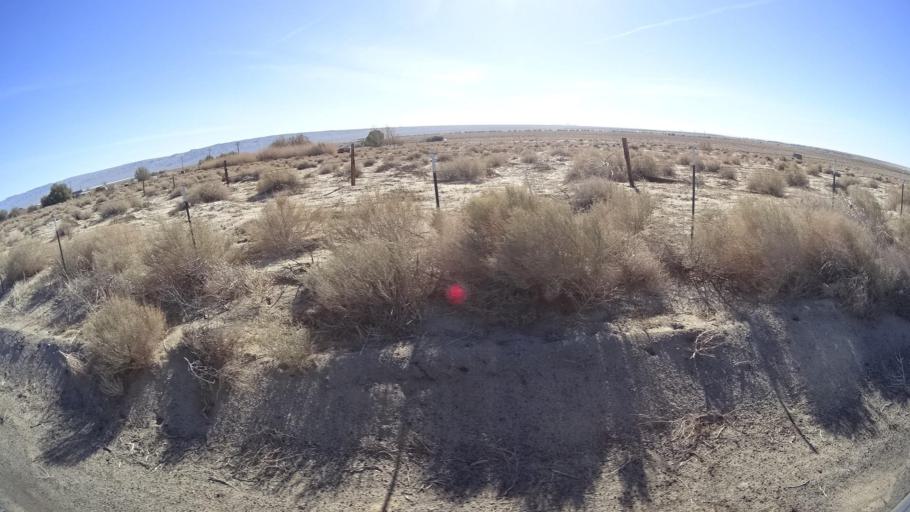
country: US
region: California
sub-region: Kern County
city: California City
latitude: 35.3066
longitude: -117.9717
